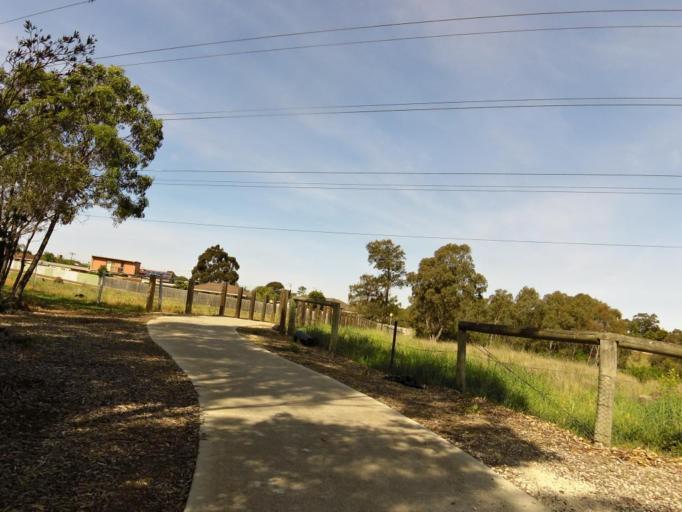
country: AU
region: Victoria
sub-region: Brimbank
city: Deer Park
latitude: -37.7585
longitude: 144.7607
